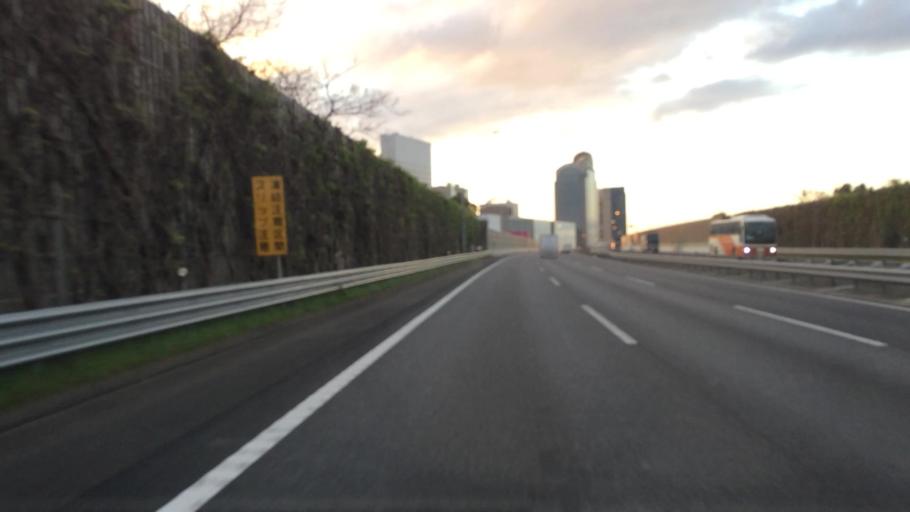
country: JP
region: Chiba
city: Funabashi
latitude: 35.6504
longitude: 140.0523
